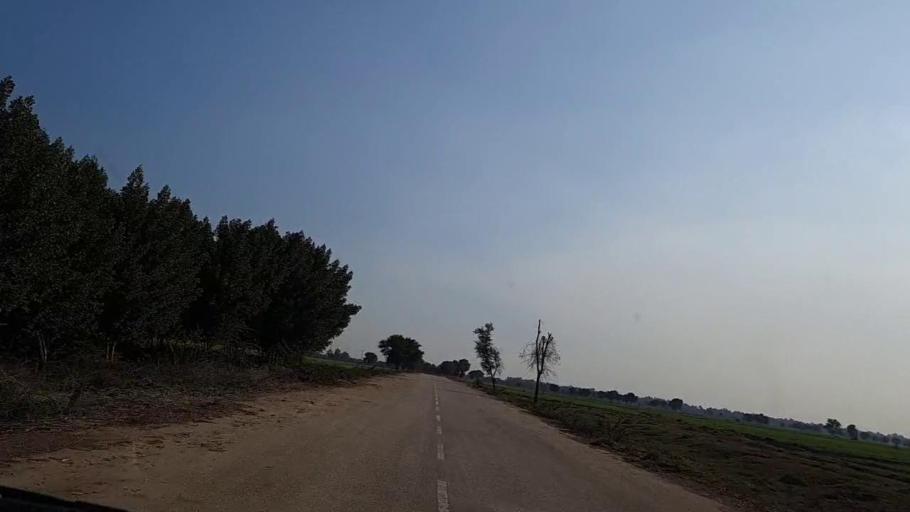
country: PK
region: Sindh
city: Sakrand
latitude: 26.1225
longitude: 68.2482
